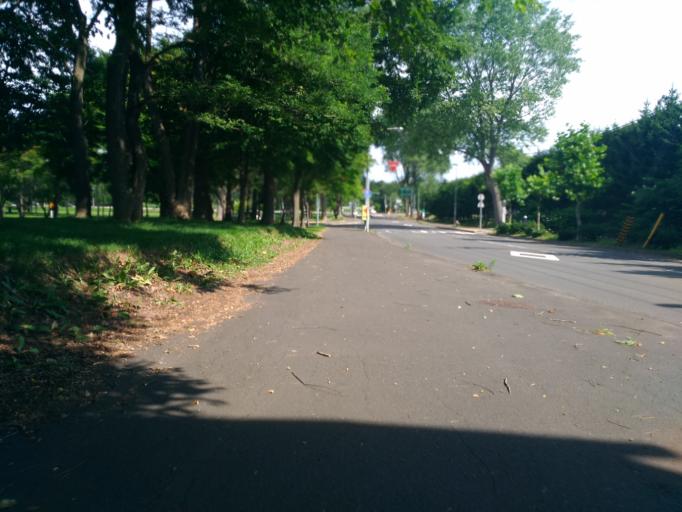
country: JP
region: Hokkaido
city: Ebetsu
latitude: 43.0712
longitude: 141.5015
